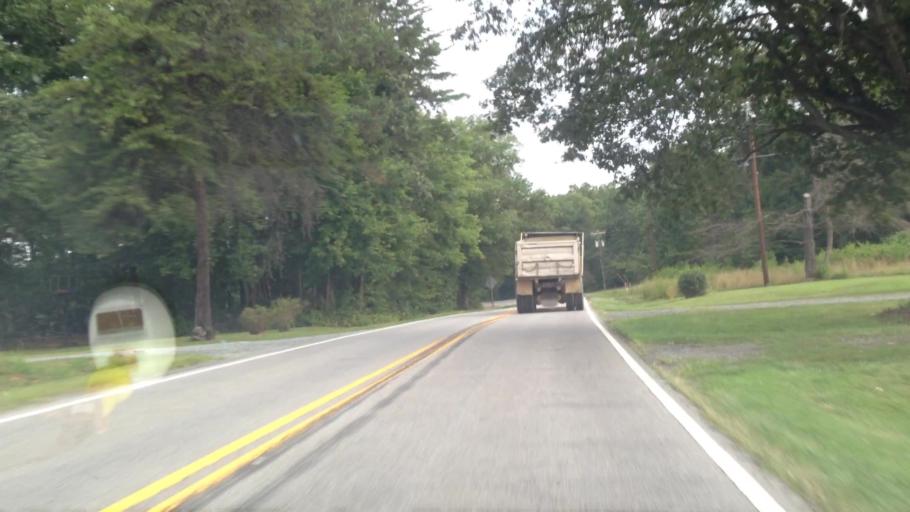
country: US
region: North Carolina
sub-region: Forsyth County
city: Walkertown
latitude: 36.1864
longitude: -80.2091
